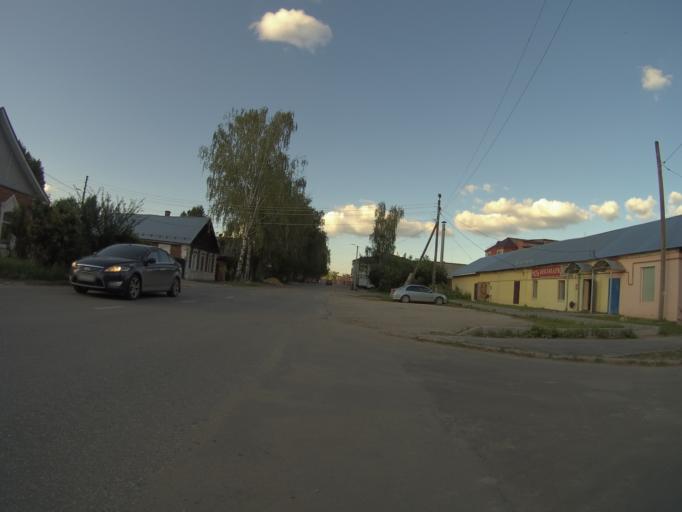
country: RU
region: Vladimir
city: Gus'-Khrustal'nyy
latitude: 55.6164
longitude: 40.6618
